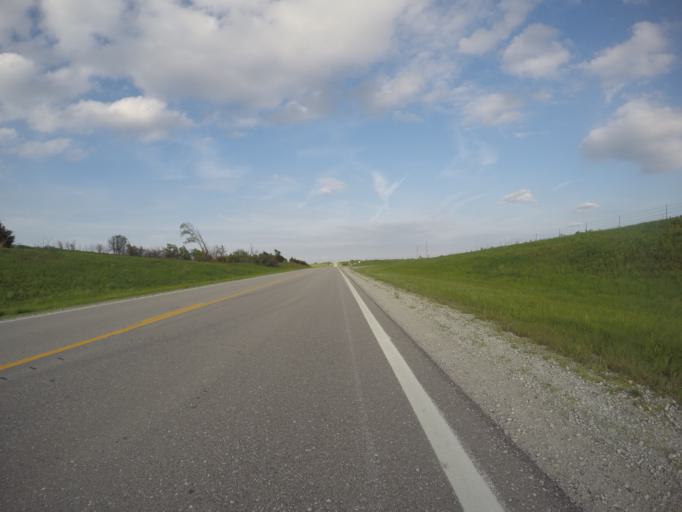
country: US
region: Kansas
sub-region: Pottawatomie County
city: Westmoreland
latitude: 39.4283
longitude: -96.5727
